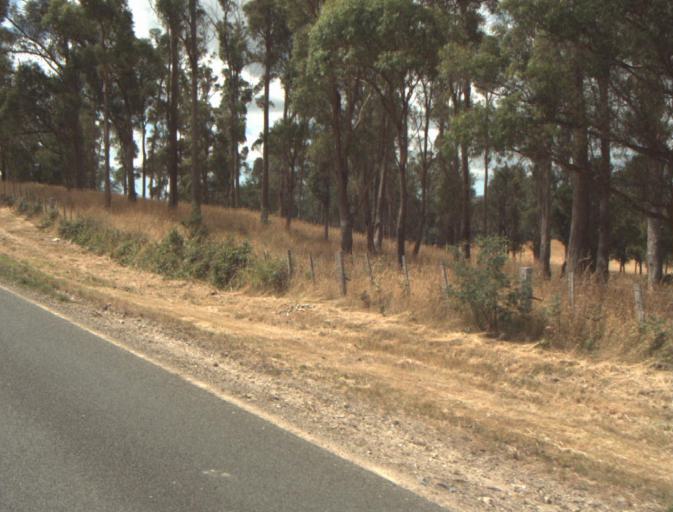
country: AU
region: Tasmania
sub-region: Launceston
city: Mayfield
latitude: -41.2209
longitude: 147.1216
